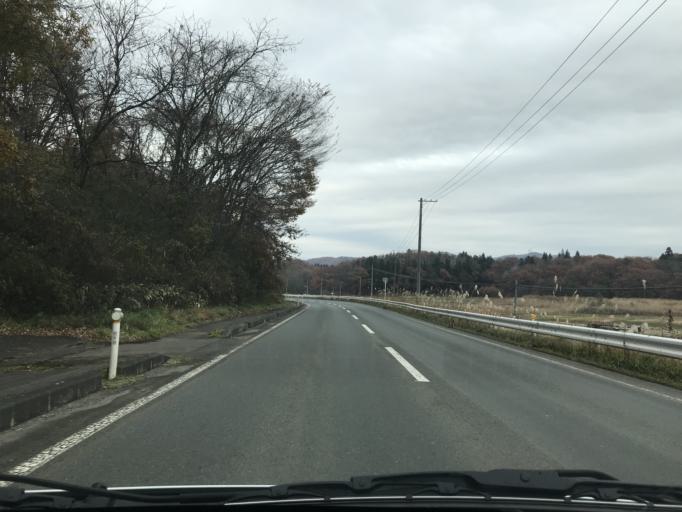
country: JP
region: Iwate
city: Kitakami
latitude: 39.2960
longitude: 141.1916
